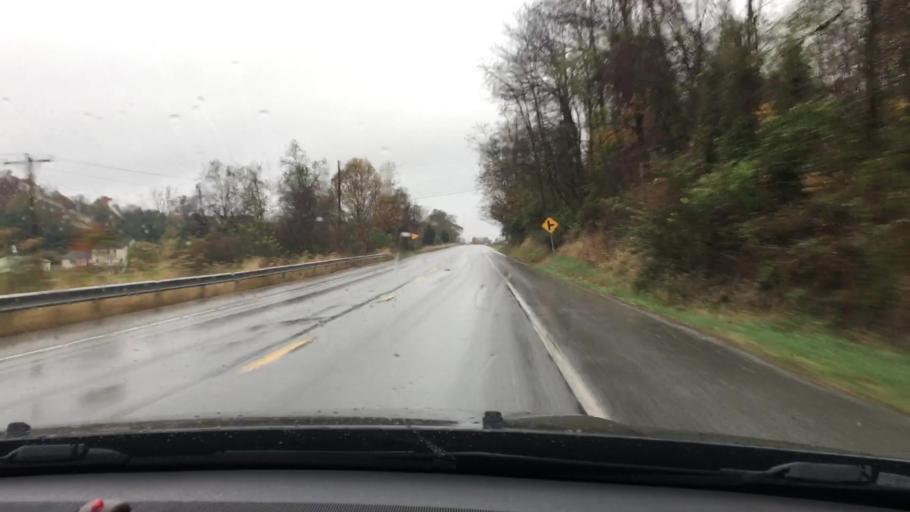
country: US
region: Pennsylvania
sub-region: Lancaster County
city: Conestoga
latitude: 39.8483
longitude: -76.2990
